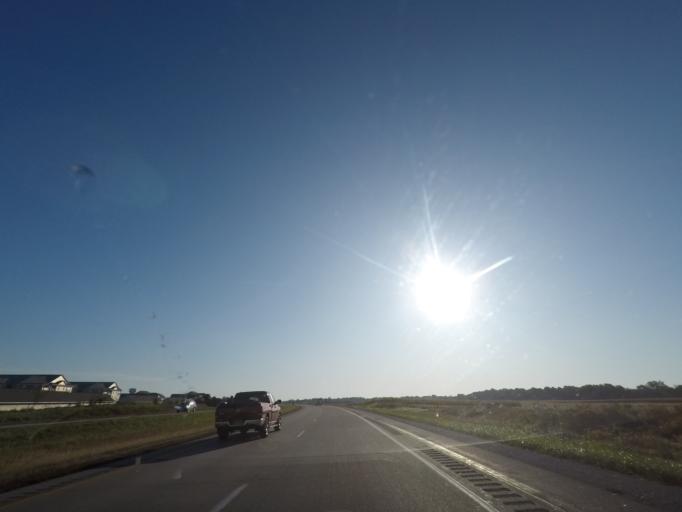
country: US
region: Iowa
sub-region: Story County
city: Ames
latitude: 42.0069
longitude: -93.6732
